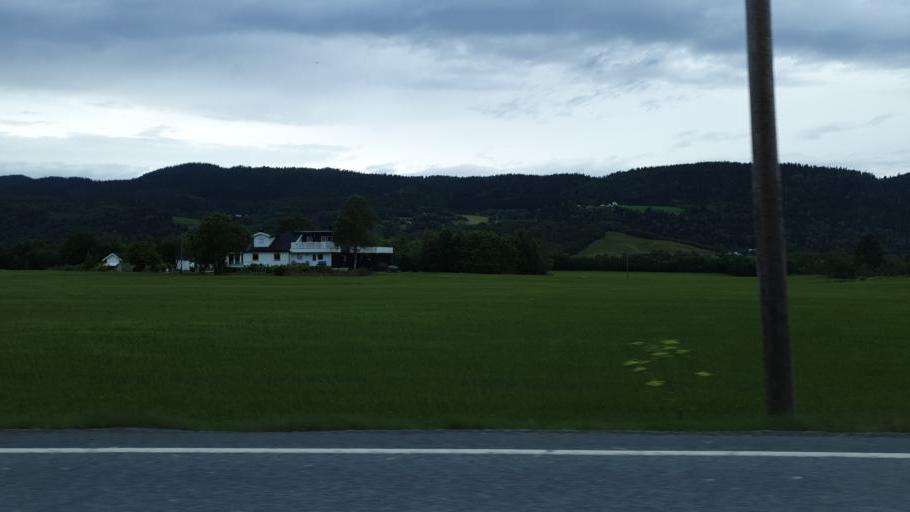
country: NO
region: Sor-Trondelag
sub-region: Melhus
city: Lundamo
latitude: 63.1717
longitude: 10.3154
